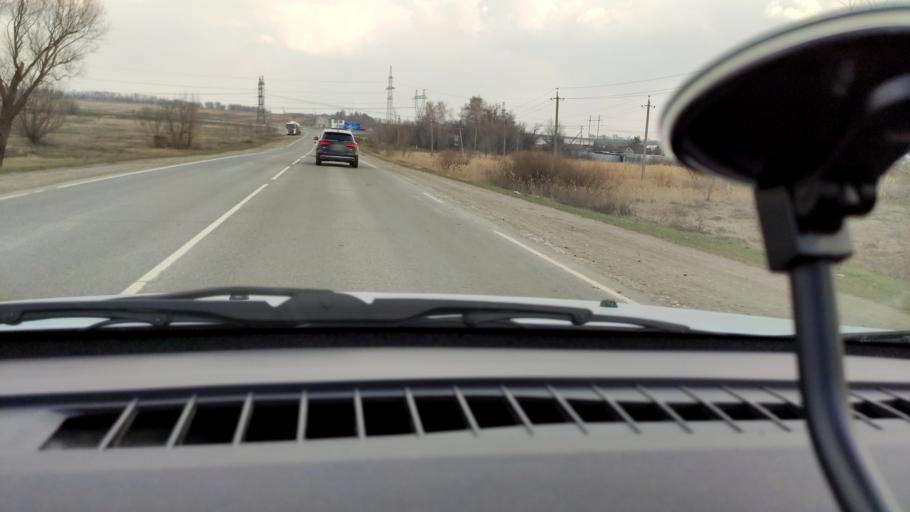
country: RU
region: Samara
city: Dubovyy Umet
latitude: 53.0646
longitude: 50.3722
